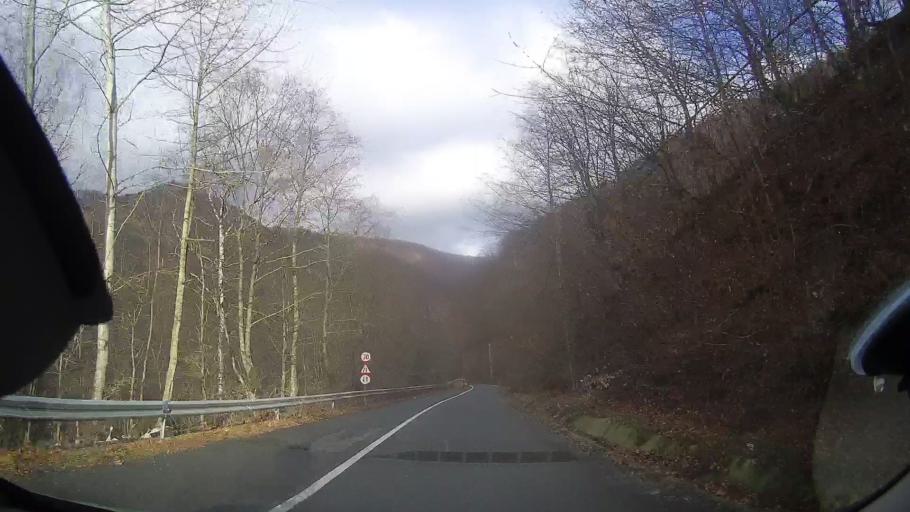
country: RO
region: Cluj
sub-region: Comuna Valea Ierii
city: Valea Ierii
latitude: 46.6879
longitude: 23.3070
